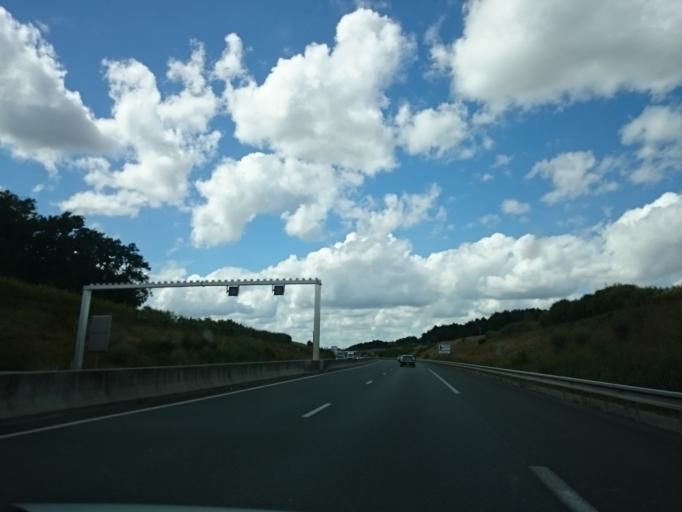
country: FR
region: Pays de la Loire
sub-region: Departement de Maine-et-Loire
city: Avrille
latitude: 47.4925
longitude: -0.5961
